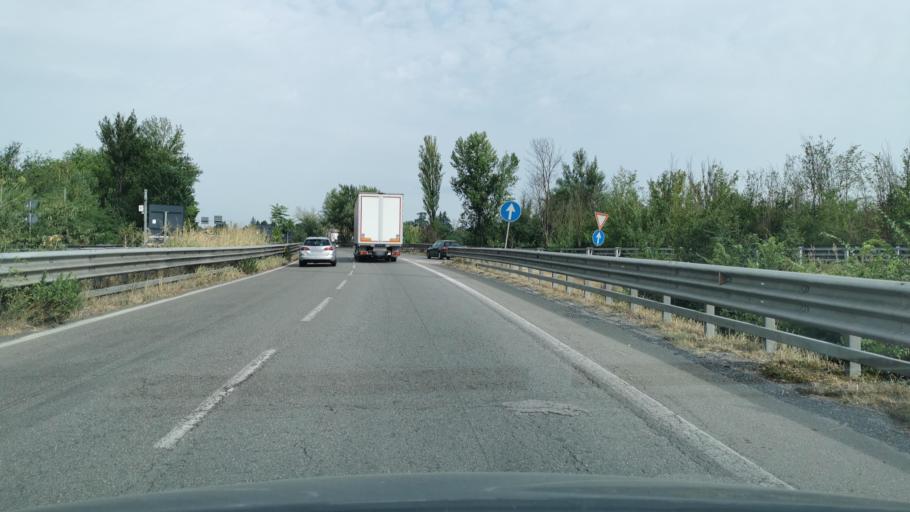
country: IT
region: Emilia-Romagna
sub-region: Provincia di Modena
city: Modena
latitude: 44.6582
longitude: 10.9534
